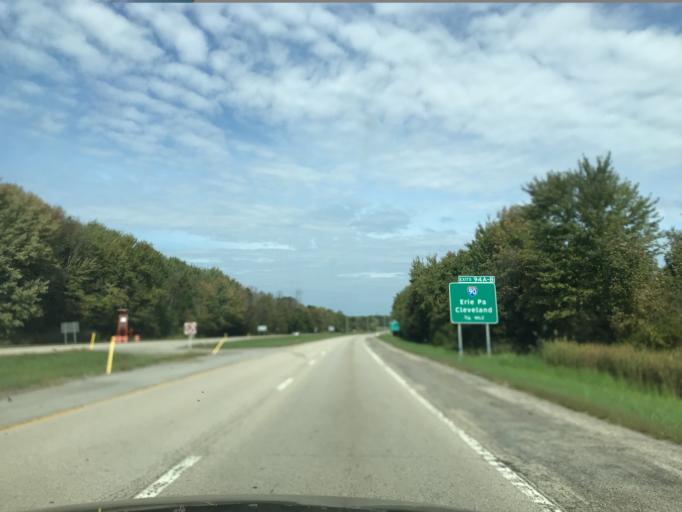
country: US
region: Ohio
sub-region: Ashtabula County
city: Ashtabula
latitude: 41.8156
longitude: -80.7625
